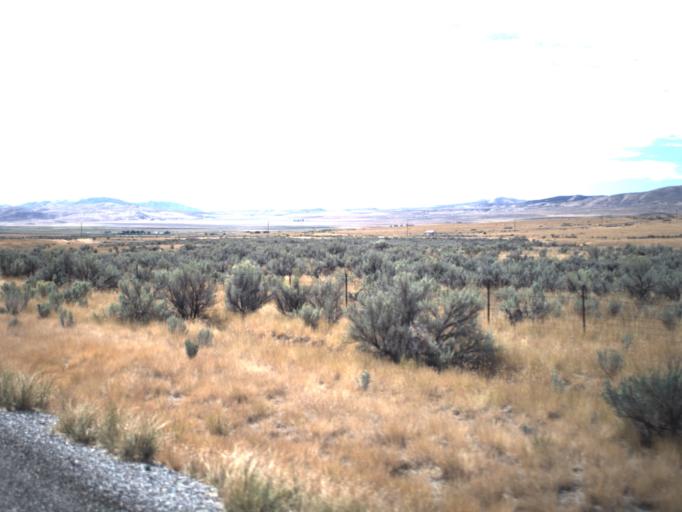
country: US
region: Utah
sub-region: Box Elder County
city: Garland
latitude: 41.7998
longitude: -112.4163
